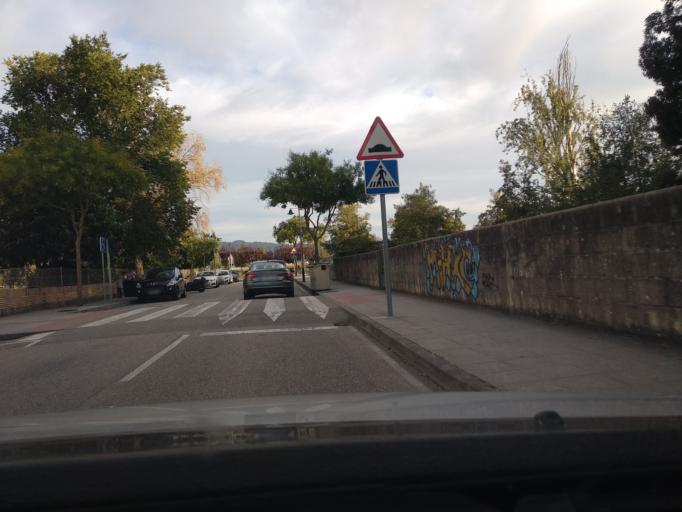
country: ES
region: Galicia
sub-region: Provincia de Pontevedra
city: Moana
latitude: 42.2883
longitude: -8.7310
